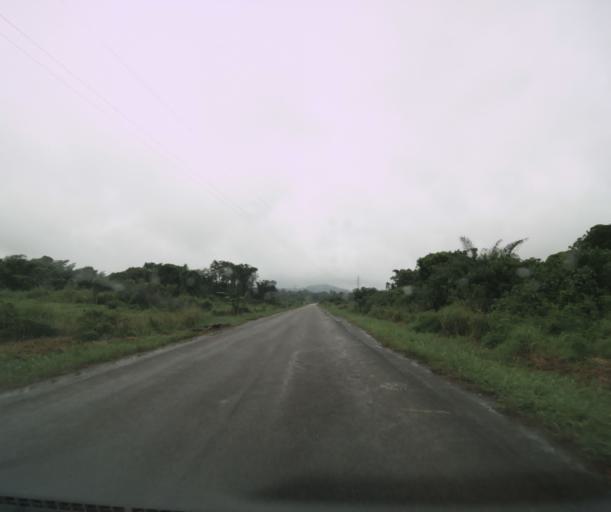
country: CM
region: Littoral
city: Edea
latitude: 3.6543
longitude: 10.1141
